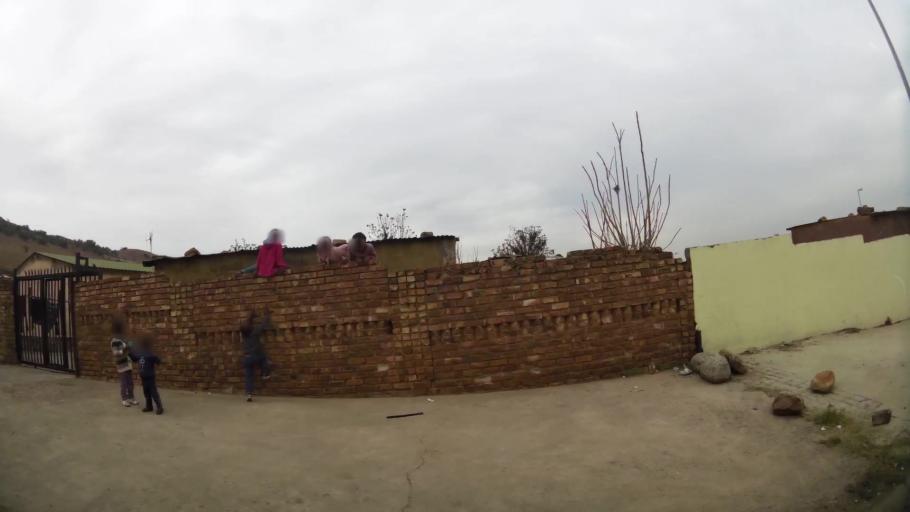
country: ZA
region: Gauteng
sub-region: City of Tshwane Metropolitan Municipality
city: Pretoria
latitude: -25.7012
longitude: 28.3341
